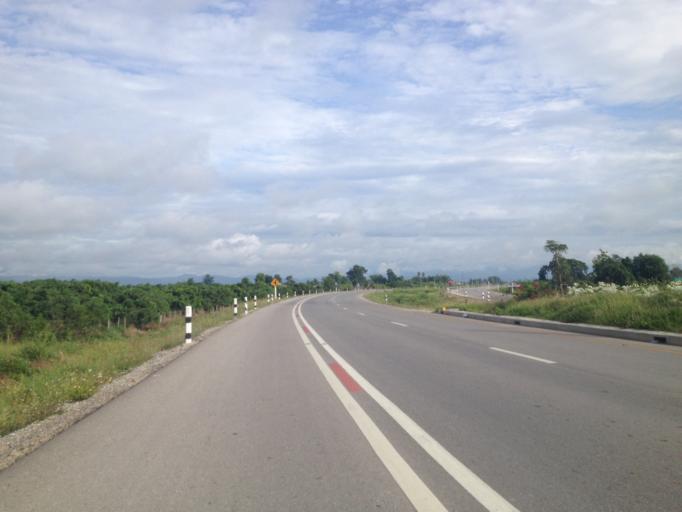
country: TH
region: Lamphun
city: Pa Sang
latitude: 18.5469
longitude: 98.8494
